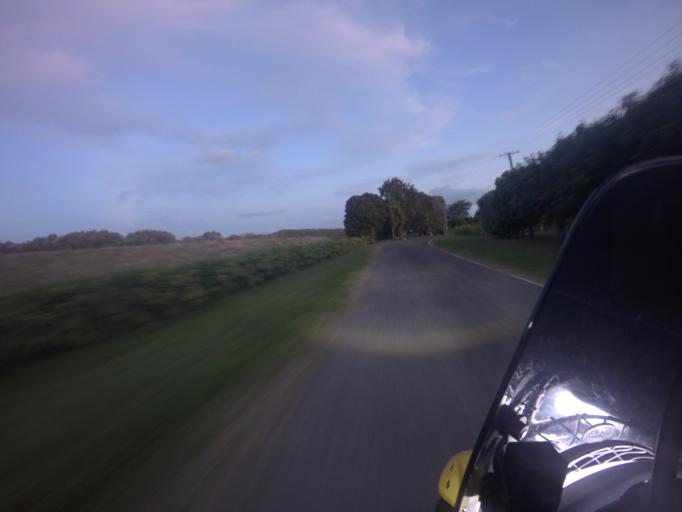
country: NZ
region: Gisborne
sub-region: Gisborne District
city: Gisborne
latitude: -38.6733
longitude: 177.9322
